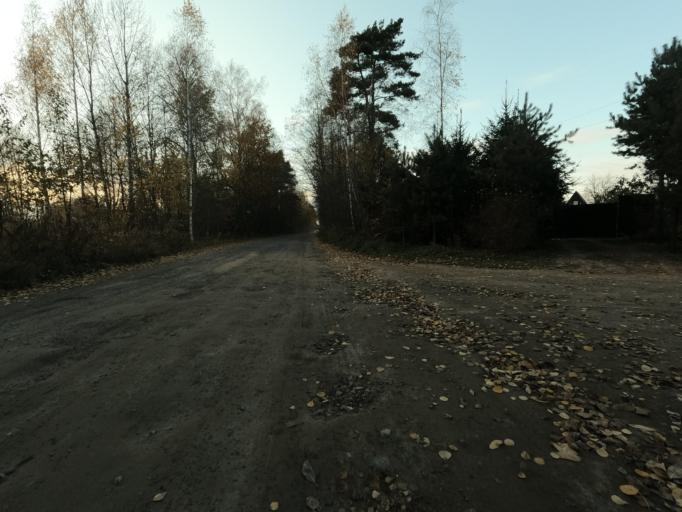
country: RU
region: Leningrad
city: Mga
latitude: 59.7615
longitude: 31.2584
